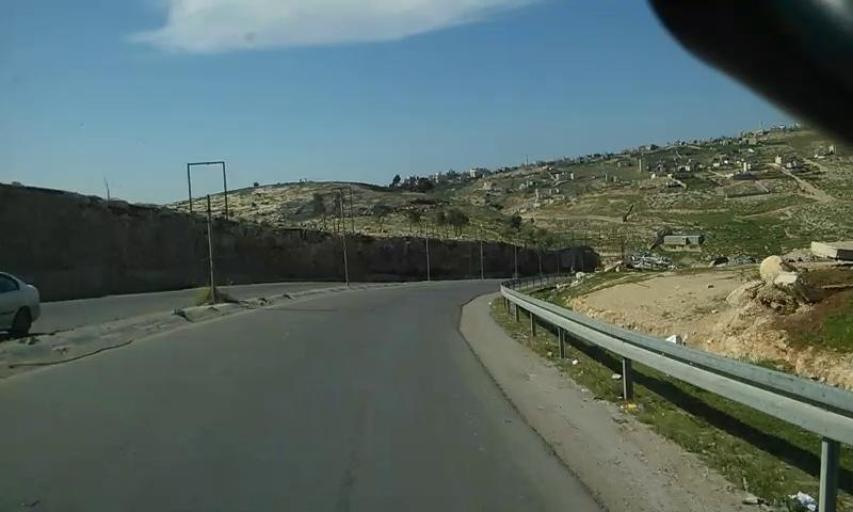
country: PS
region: West Bank
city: Abu Dis
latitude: 31.7543
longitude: 35.2788
